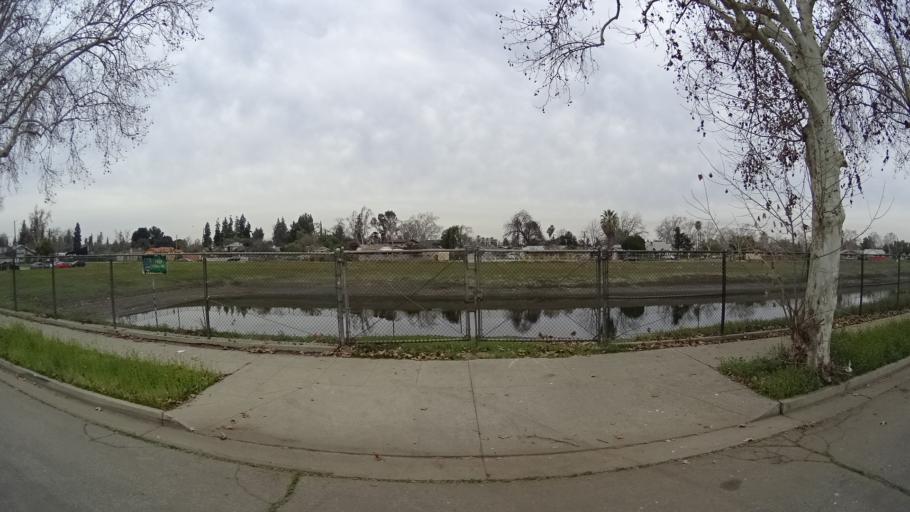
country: US
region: California
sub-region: Fresno County
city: Fresno
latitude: 36.7334
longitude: -119.7750
